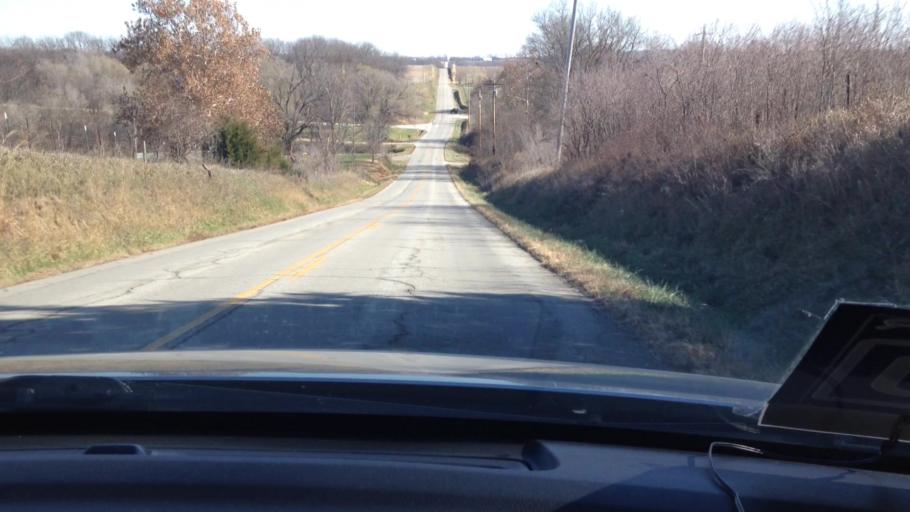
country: US
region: Missouri
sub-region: Platte County
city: Weston
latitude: 39.4982
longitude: -94.8203
